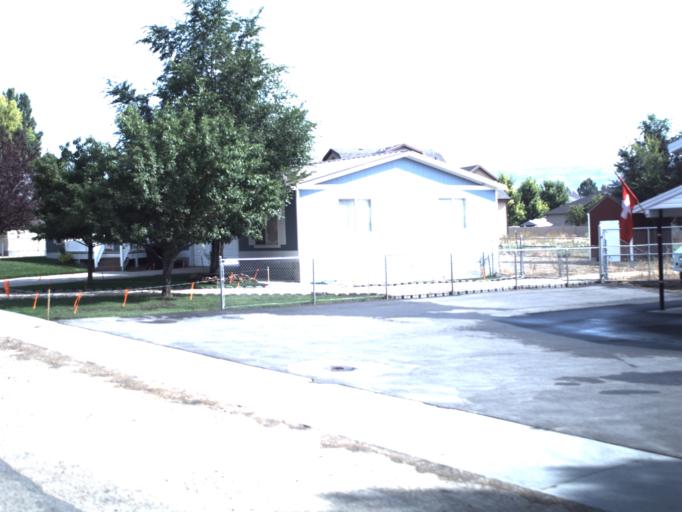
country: US
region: Utah
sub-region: Wasatch County
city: Midway
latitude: 40.5078
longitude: -111.4724
